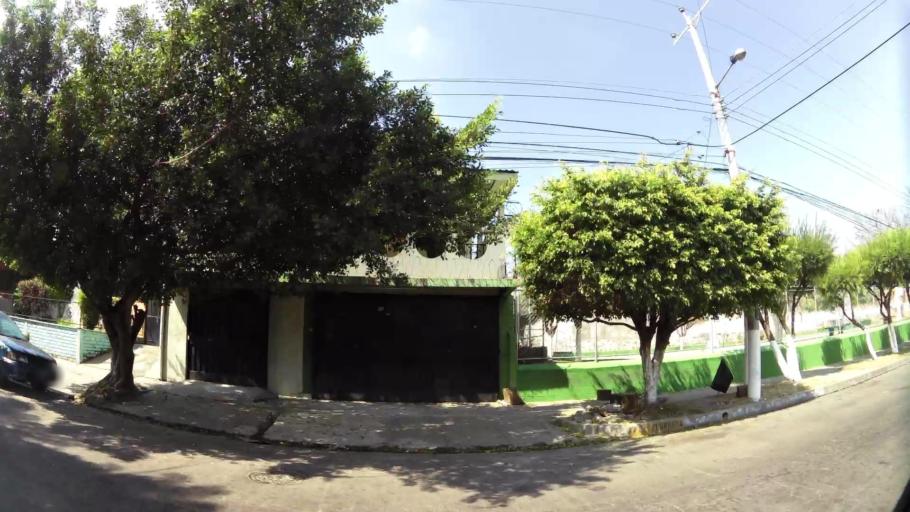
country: SV
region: San Salvador
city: San Salvador
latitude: 13.6867
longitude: -89.2215
